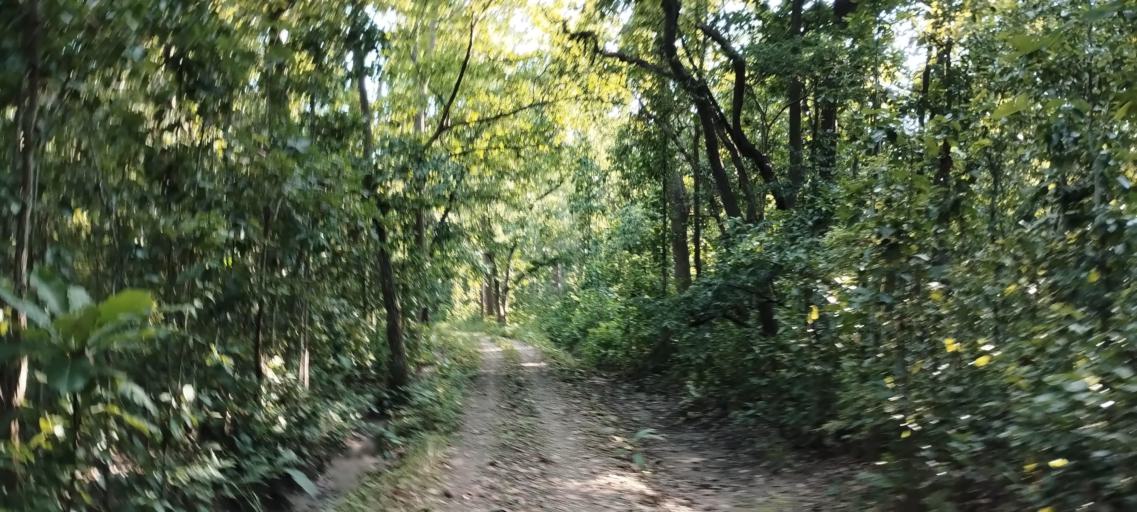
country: NP
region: Far Western
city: Tikapur
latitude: 28.5063
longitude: 81.2664
